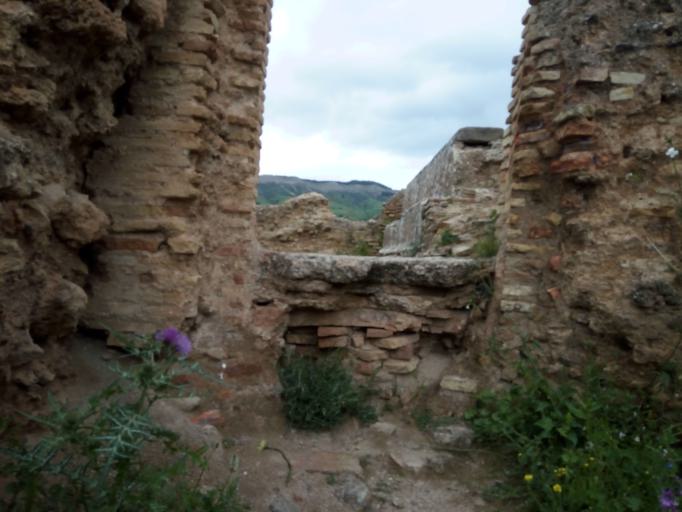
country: DZ
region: Setif
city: El Eulma
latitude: 36.3229
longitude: 5.7350
